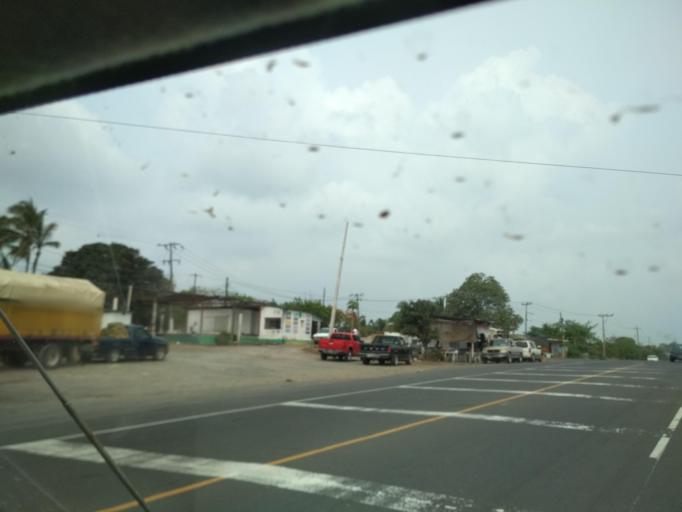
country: MX
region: Veracruz
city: Paso del Toro
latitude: 19.0053
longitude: -96.1117
